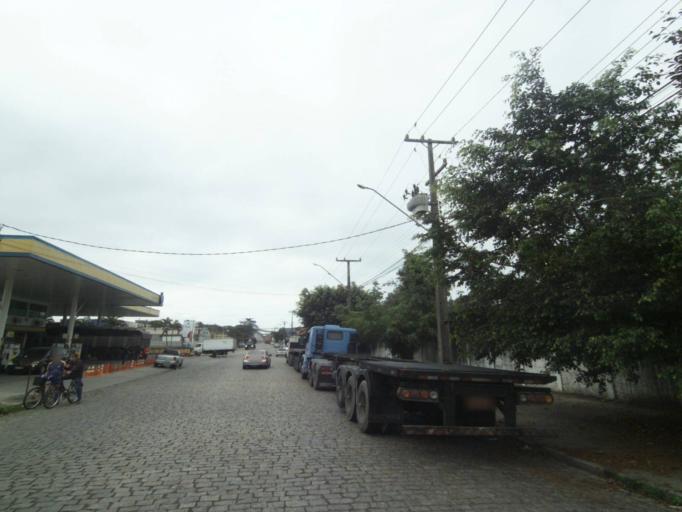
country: BR
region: Parana
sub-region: Paranagua
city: Paranagua
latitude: -25.5138
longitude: -48.5176
